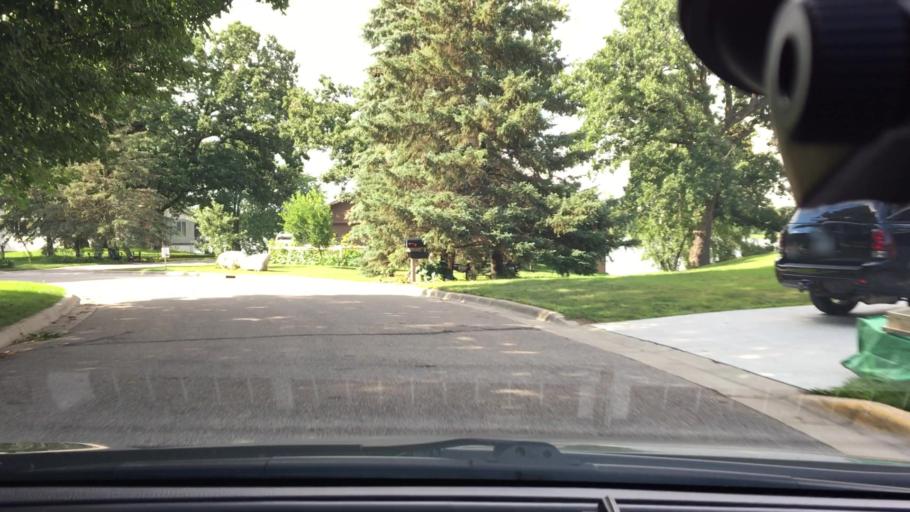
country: US
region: Minnesota
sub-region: Carver County
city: Victoria
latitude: 44.8610
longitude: -93.6798
